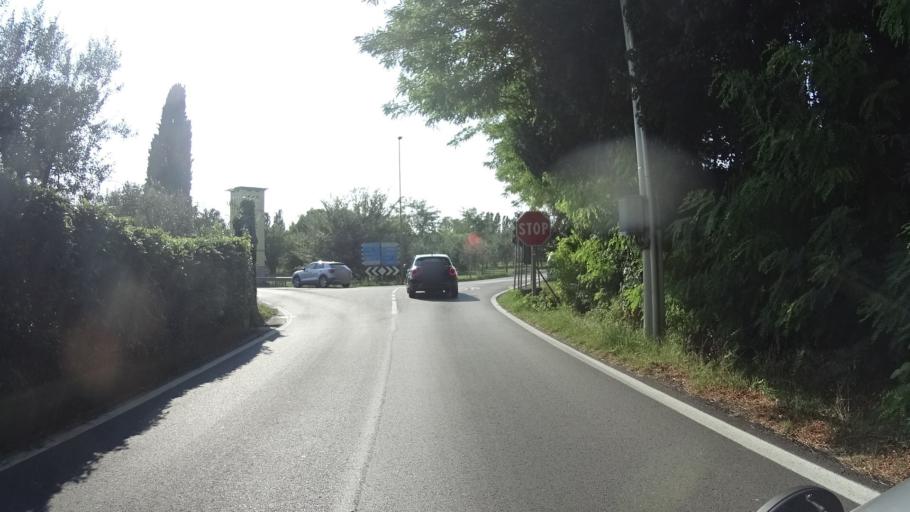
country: IT
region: Veneto
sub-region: Provincia di Verona
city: Lazise
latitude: 45.5083
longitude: 10.7452
